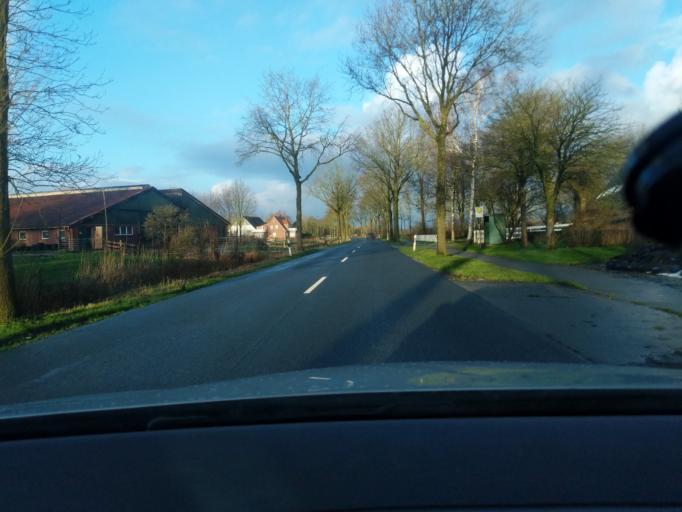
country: DE
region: Lower Saxony
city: Cuxhaven
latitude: 53.8337
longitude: 8.7025
